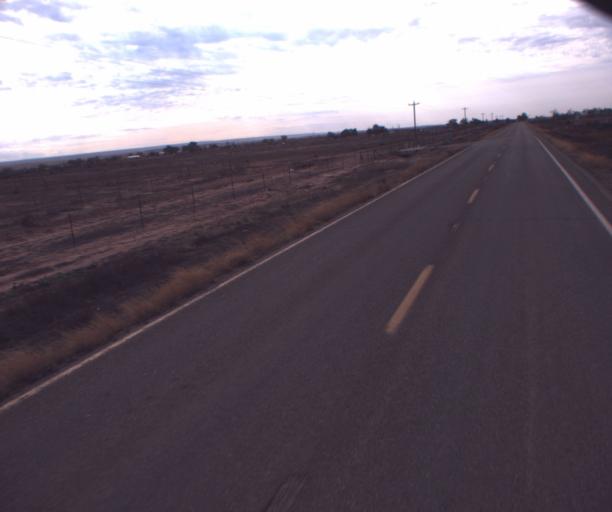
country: US
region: Arizona
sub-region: Apache County
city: Many Farms
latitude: 36.4295
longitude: -109.6067
